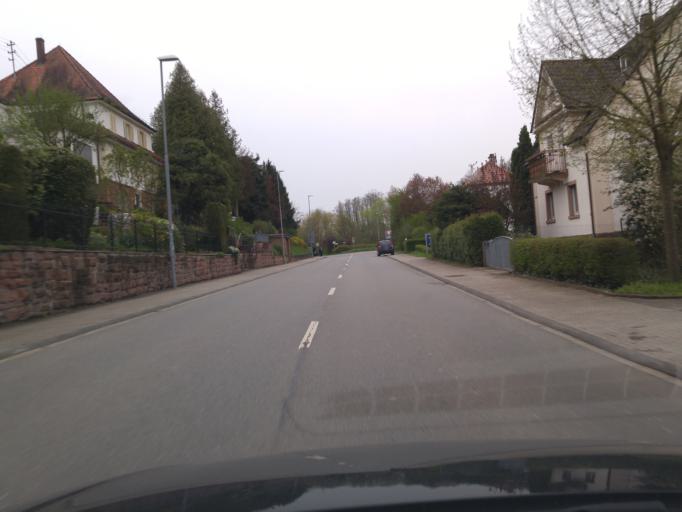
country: DE
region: Baden-Wuerttemberg
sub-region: Karlsruhe Region
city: Aglasterhausen
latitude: 49.3526
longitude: 8.9955
